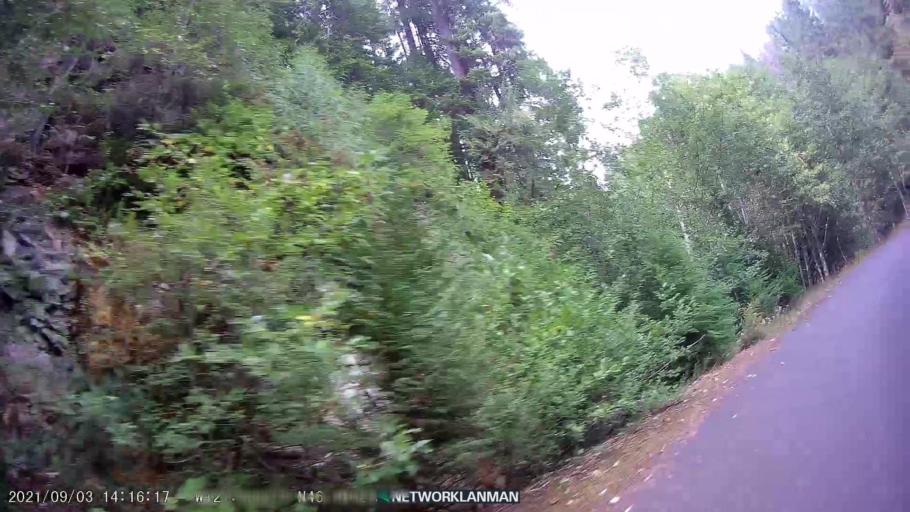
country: US
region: Washington
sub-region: Skamania County
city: Carson
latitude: 46.1914
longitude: -121.8554
